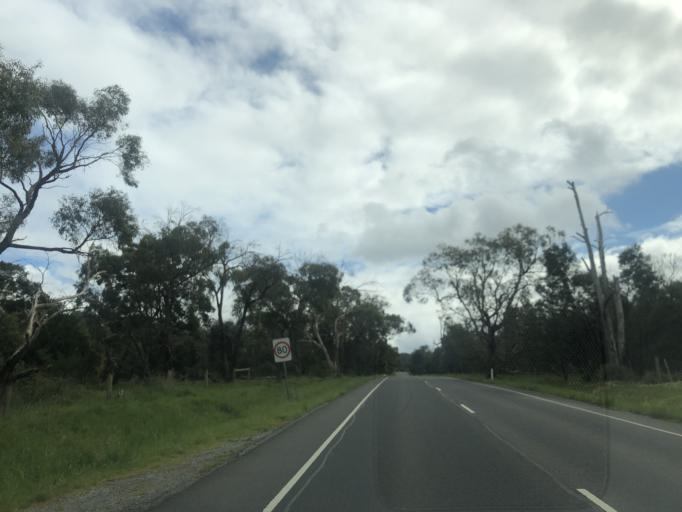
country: AU
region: Victoria
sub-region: Casey
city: Endeavour Hills
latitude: -37.9594
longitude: 145.2494
